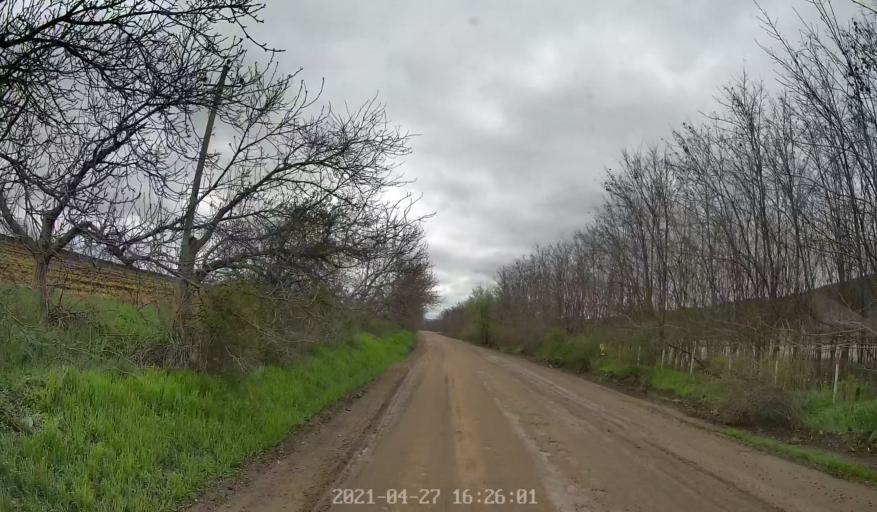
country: MD
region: Chisinau
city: Singera
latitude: 46.9818
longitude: 29.0228
